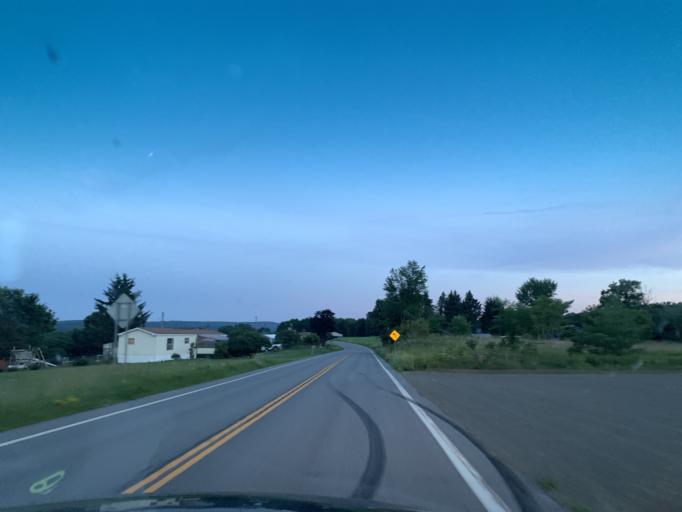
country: US
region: New York
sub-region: Chenango County
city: New Berlin
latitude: 42.6516
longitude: -75.3320
